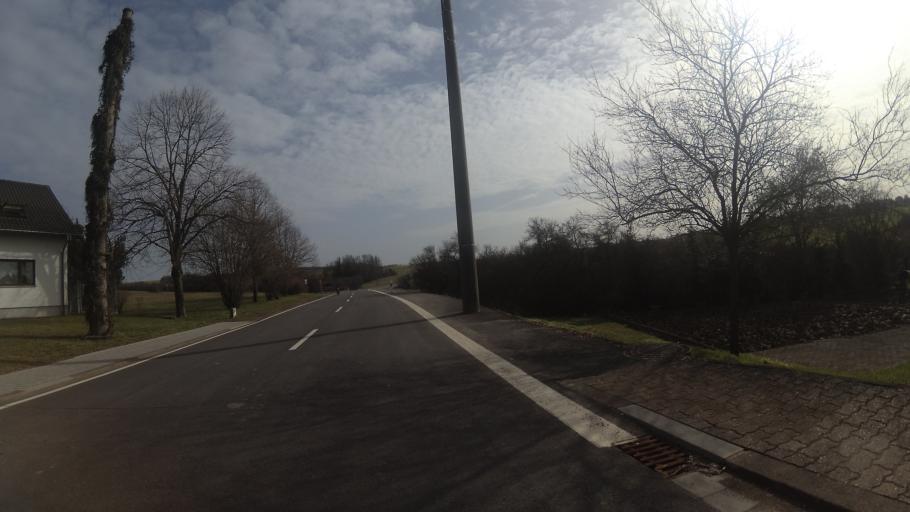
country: FR
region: Lorraine
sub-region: Departement de la Moselle
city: Merten
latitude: 49.3028
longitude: 6.6644
